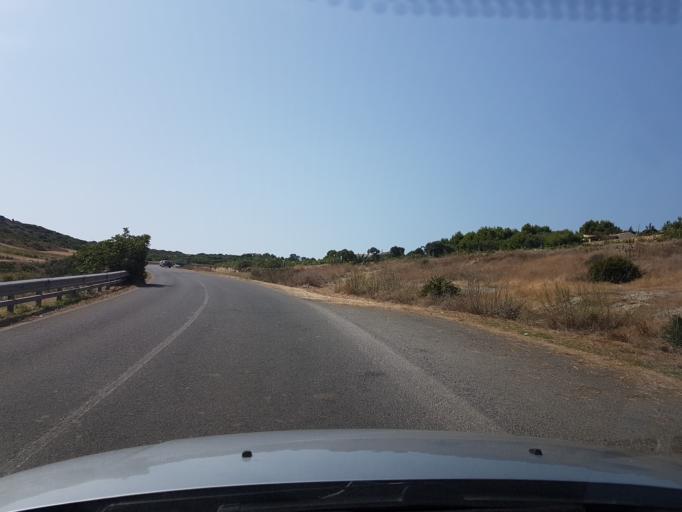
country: IT
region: Sardinia
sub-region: Provincia di Oristano
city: Cabras
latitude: 39.9312
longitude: 8.4516
